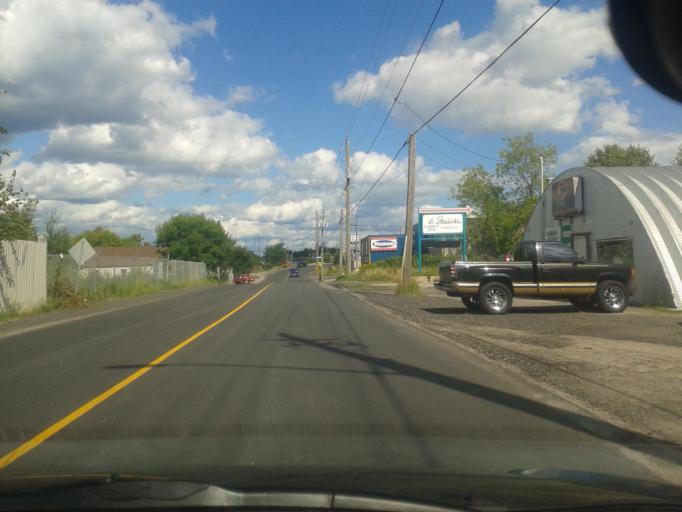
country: CA
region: Ontario
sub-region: Nipissing District
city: North Bay
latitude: 46.3096
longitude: -79.4430
